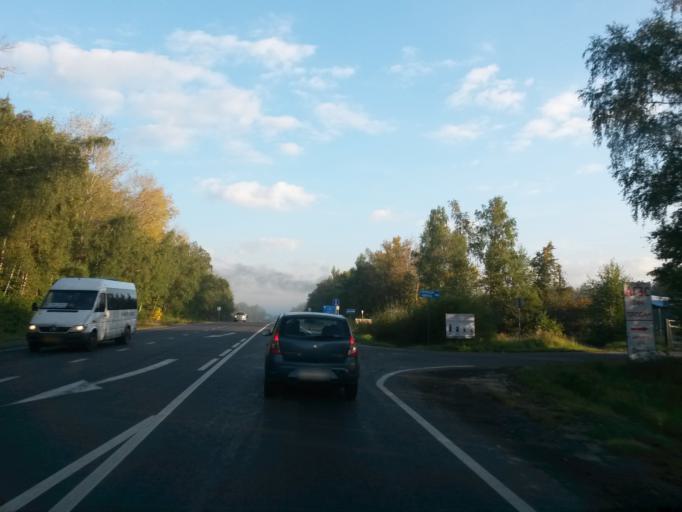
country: RU
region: Moskovskaya
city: Belyye Stolby
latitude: 55.3439
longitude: 37.7994
